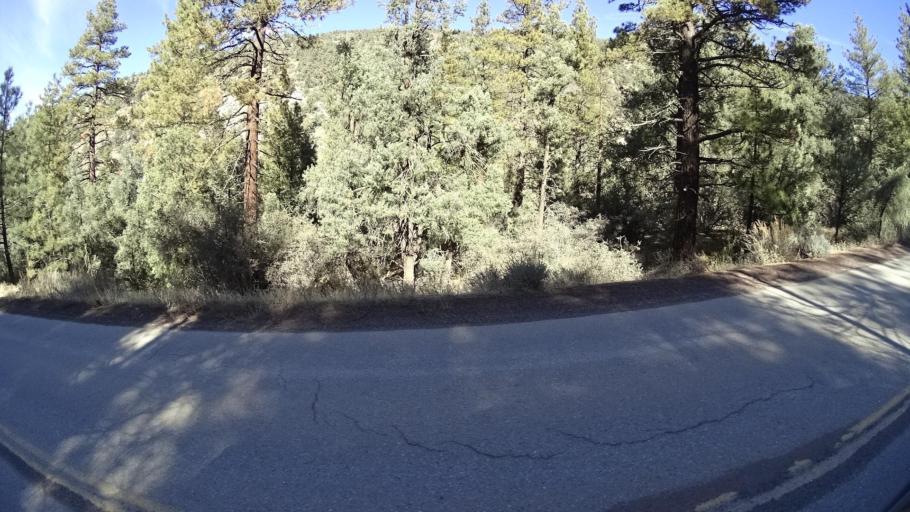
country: US
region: California
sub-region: Kern County
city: Pine Mountain Club
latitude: 34.8493
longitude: -119.0996
